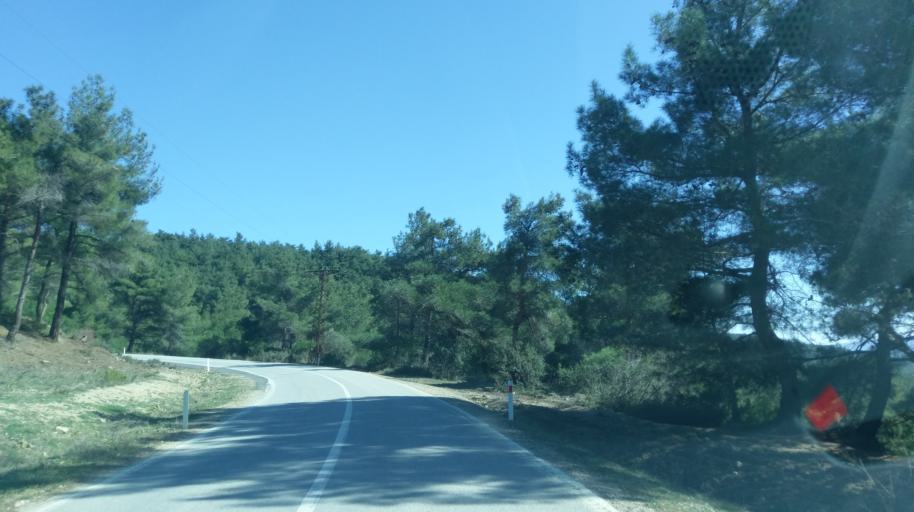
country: TR
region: Canakkale
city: Eceabat
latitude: 40.1237
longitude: 26.2935
